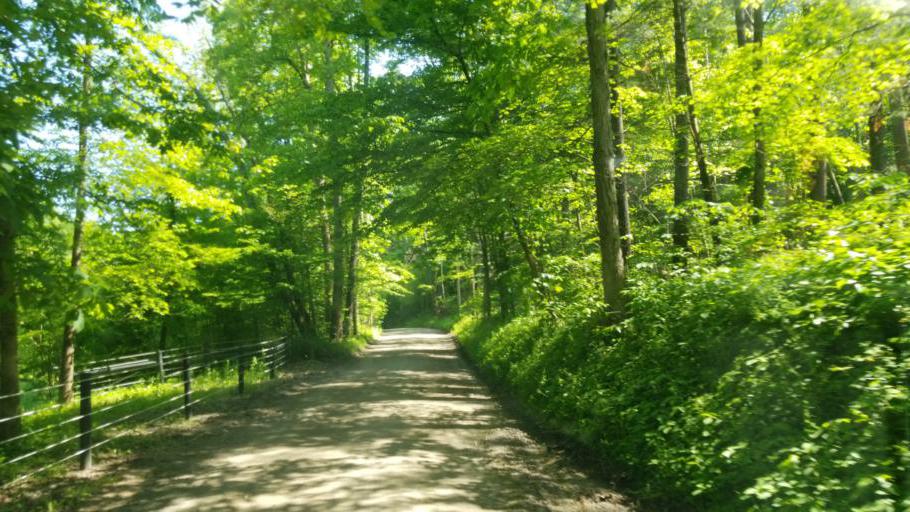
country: US
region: Ohio
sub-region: Holmes County
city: Millersburg
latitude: 40.4477
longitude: -81.8054
